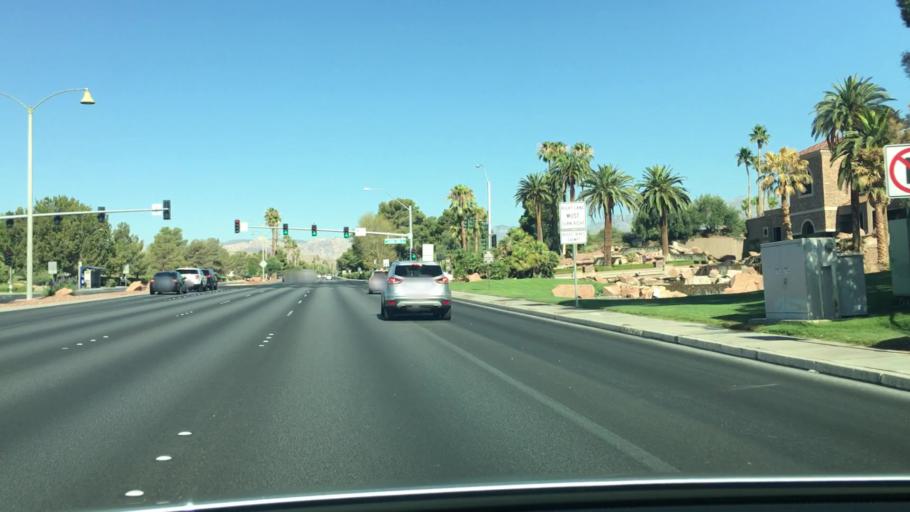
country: US
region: Nevada
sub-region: Clark County
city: Spring Valley
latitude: 36.1442
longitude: -115.2817
